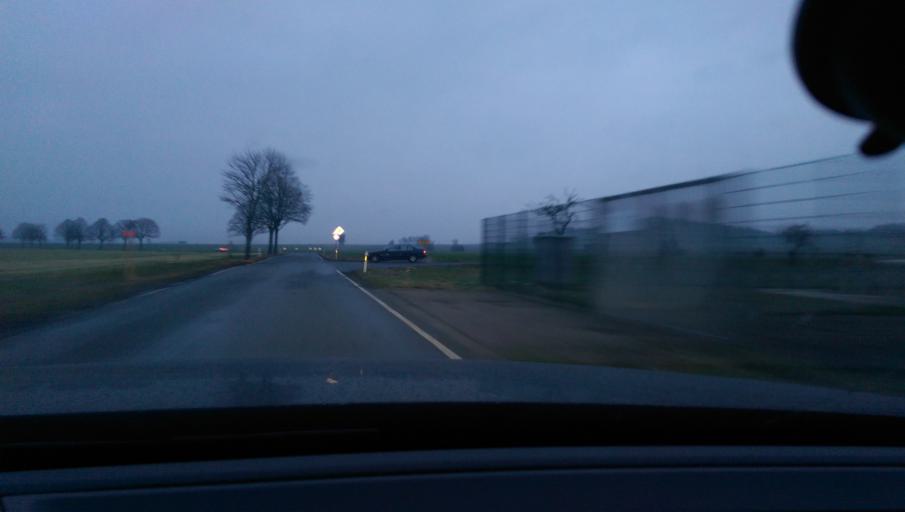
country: DE
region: Lower Saxony
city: Wennigsen
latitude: 52.3024
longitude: 9.5682
